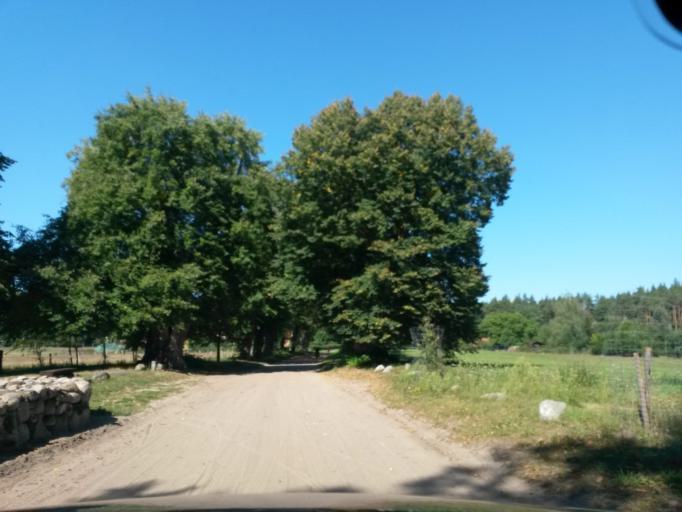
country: DE
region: Brandenburg
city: Lychen
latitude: 53.1597
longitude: 13.4053
